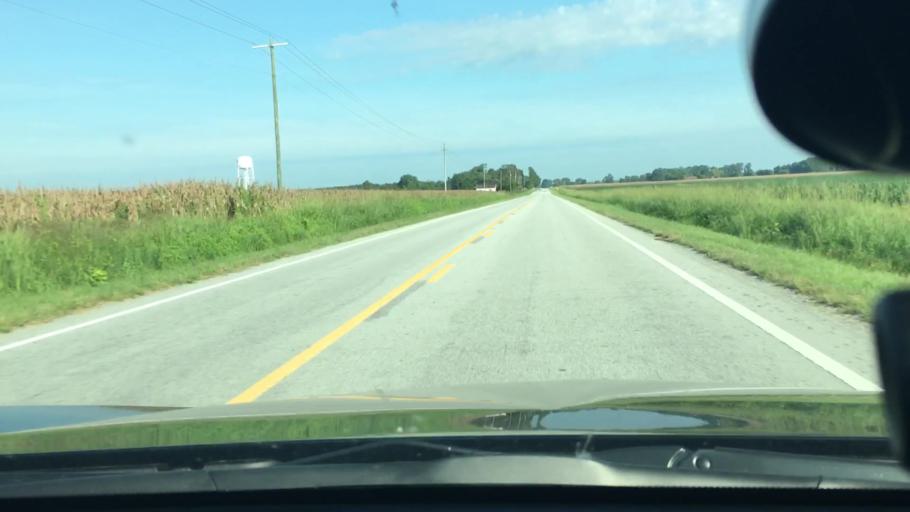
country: US
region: North Carolina
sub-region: Pitt County
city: Summerfield
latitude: 35.6508
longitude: -77.4643
